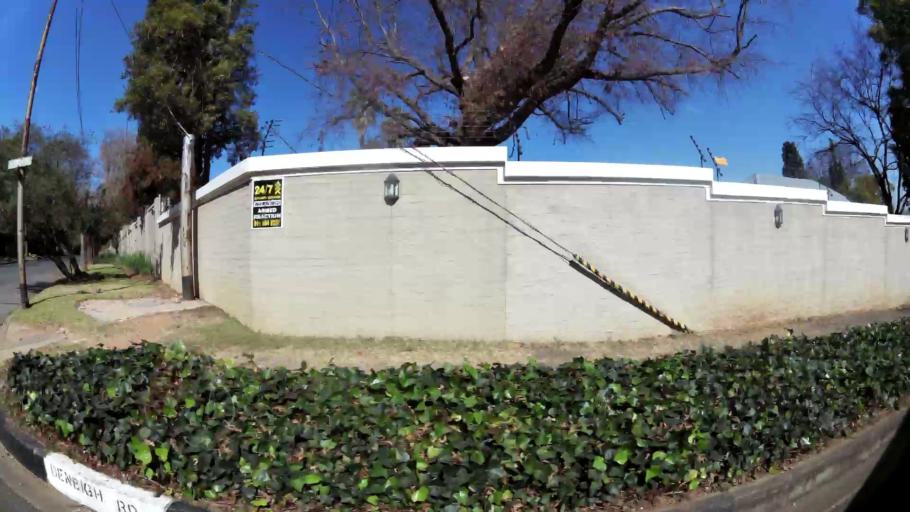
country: ZA
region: Gauteng
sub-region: City of Johannesburg Metropolitan Municipality
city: Johannesburg
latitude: -26.1515
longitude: 28.0260
